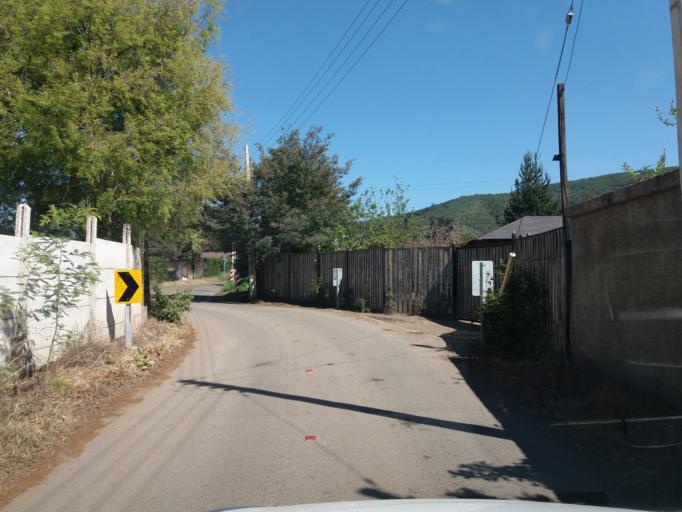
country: CL
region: Valparaiso
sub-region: Provincia de Quillota
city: Quillota
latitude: -32.8588
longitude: -71.2682
